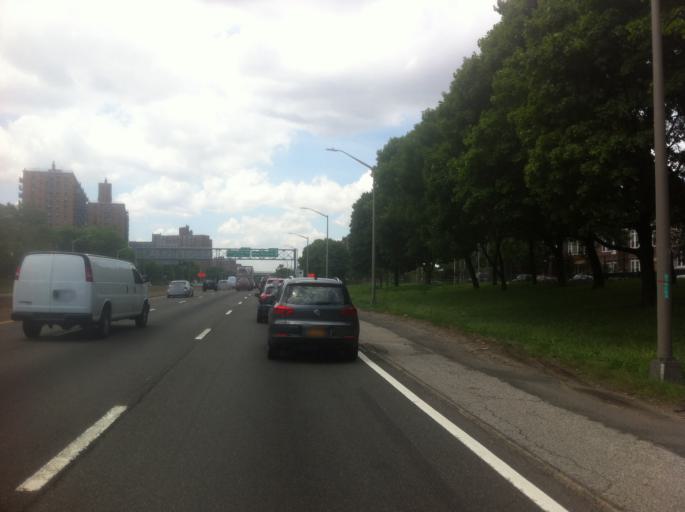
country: US
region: New York
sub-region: Bronx
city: The Bronx
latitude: 40.8271
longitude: -73.8514
